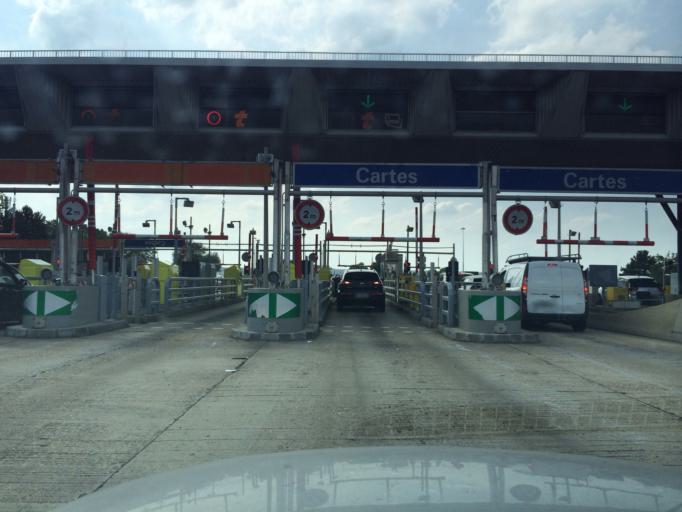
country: FR
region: Ile-de-France
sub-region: Departement des Yvelines
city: Buchelay
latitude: 48.9837
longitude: 1.6814
